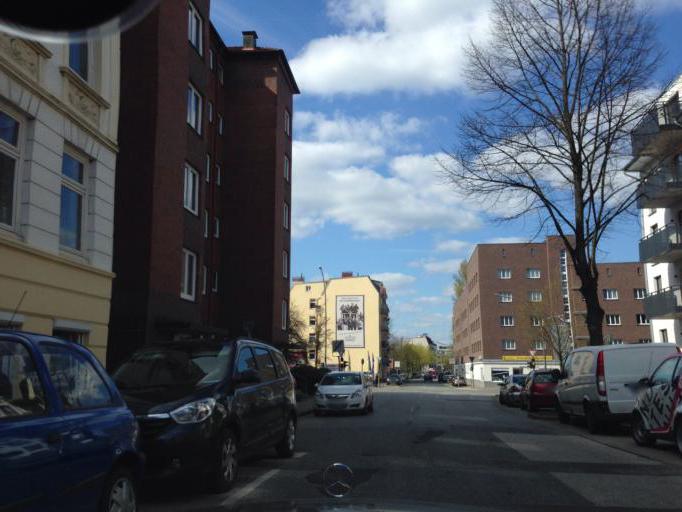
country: DE
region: Hamburg
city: Marienthal
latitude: 53.5770
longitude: 10.0873
